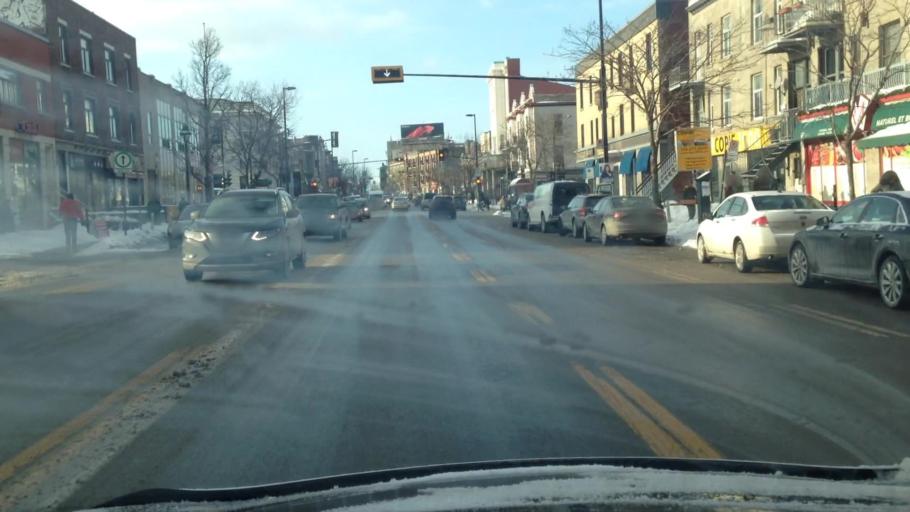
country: CA
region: Quebec
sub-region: Montreal
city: Montreal
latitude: 45.5192
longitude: -73.5948
